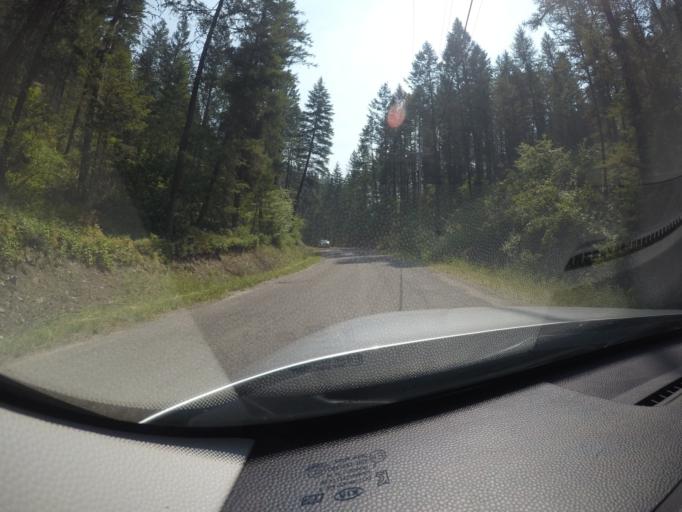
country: US
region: Montana
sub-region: Lake County
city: Polson
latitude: 47.7757
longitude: -114.1709
